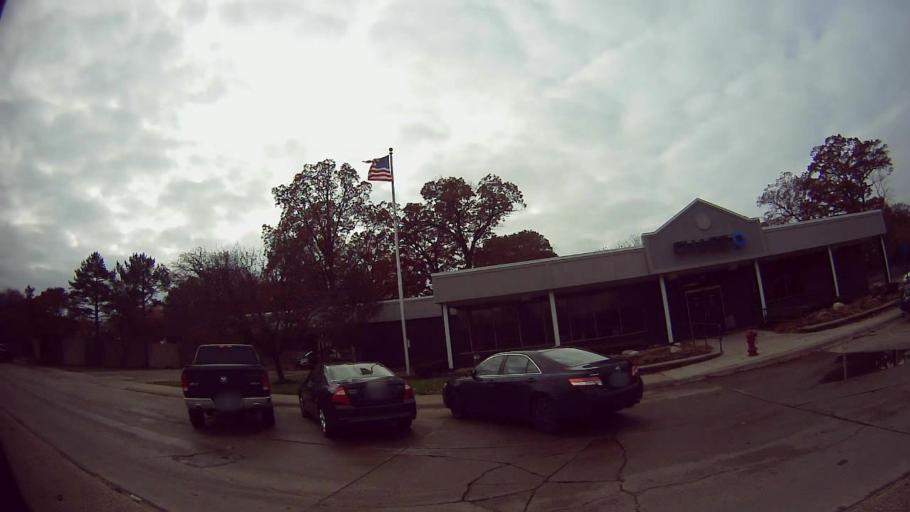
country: US
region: Michigan
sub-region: Oakland County
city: Royal Oak
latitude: 42.4854
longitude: -83.1552
